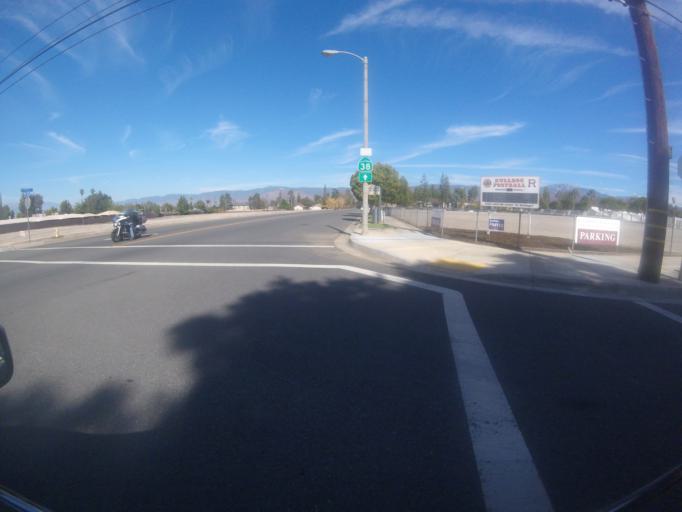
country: US
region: California
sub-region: San Bernardino County
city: Redlands
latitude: 34.0664
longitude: -117.1671
